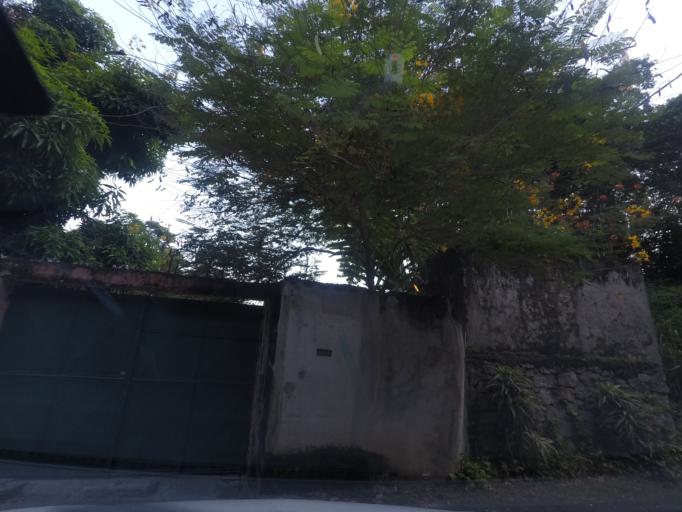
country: BR
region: Rio de Janeiro
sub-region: Rio De Janeiro
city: Rio de Janeiro
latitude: -22.9444
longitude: -43.1915
